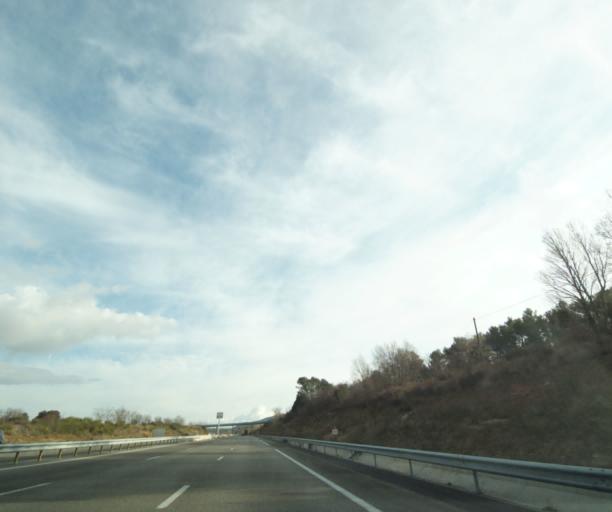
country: FR
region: Provence-Alpes-Cote d'Azur
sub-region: Departement du Var
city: Pourrieres
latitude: 43.4763
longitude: 5.7820
